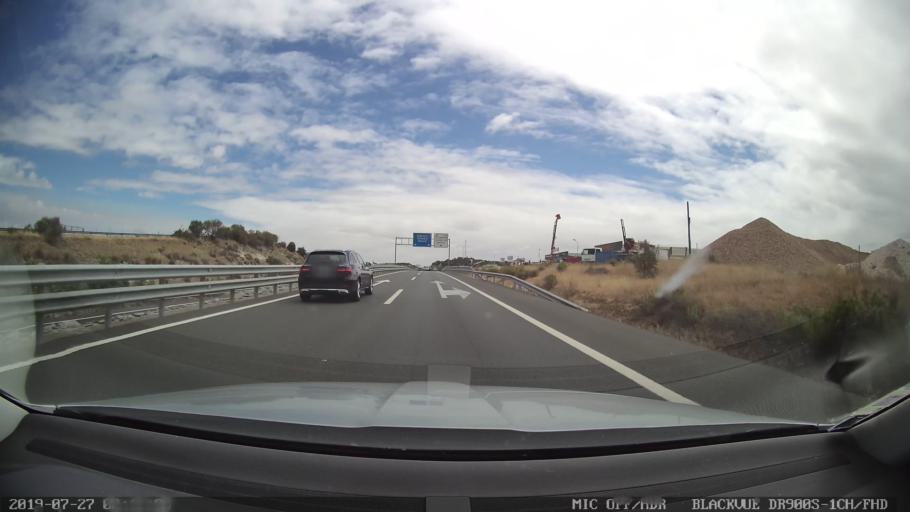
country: ES
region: Extremadura
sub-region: Provincia de Caceres
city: Peraleda de la Mata
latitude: 39.8888
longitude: -5.4718
